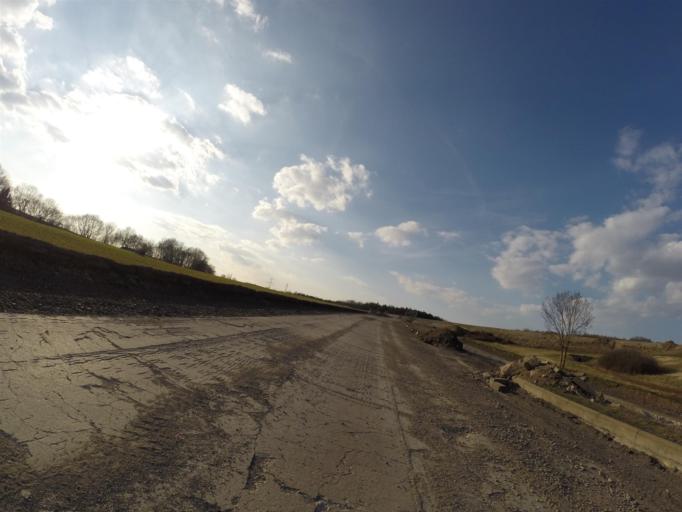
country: DE
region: Thuringia
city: Milda
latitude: 50.8749
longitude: 11.4755
